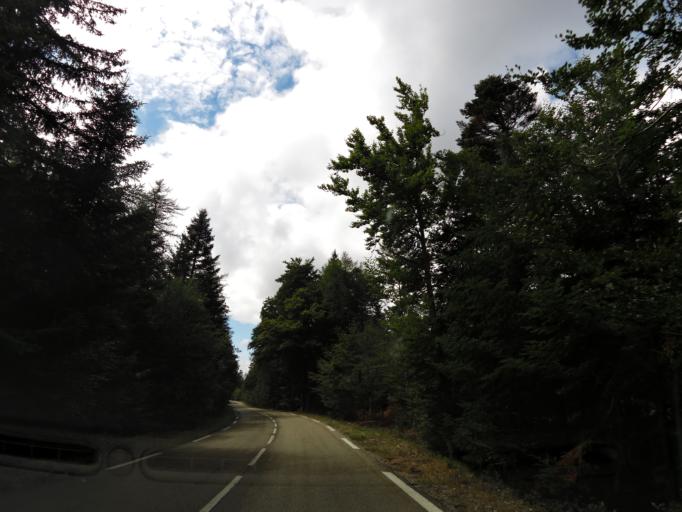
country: FR
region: Languedoc-Roussillon
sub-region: Departement de la Lozere
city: Meyrueis
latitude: 44.1040
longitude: 3.5158
